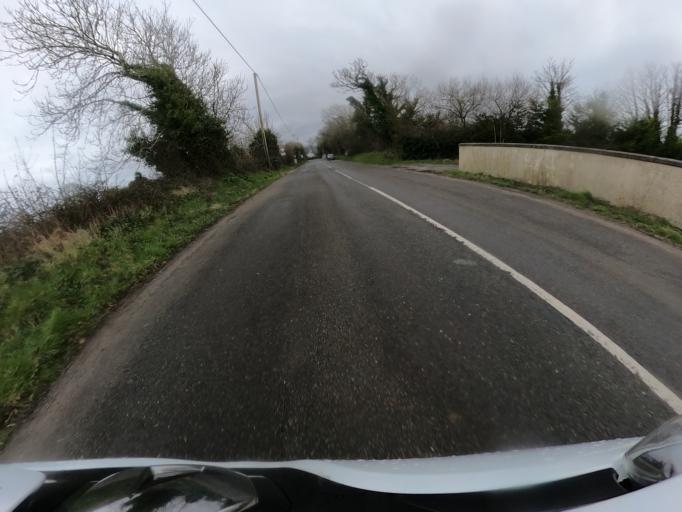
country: IM
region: Ramsey
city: Ramsey
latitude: 54.3474
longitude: -4.5041
